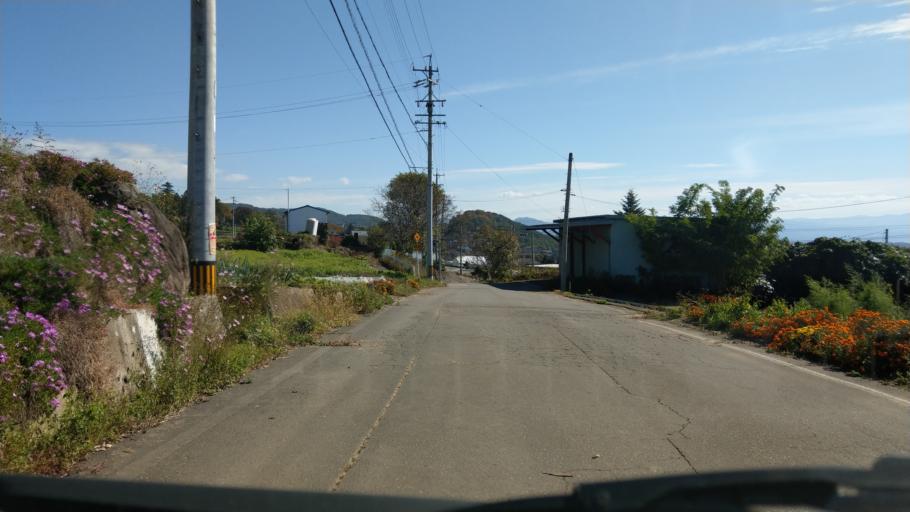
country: JP
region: Nagano
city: Komoro
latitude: 36.3520
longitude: 138.4048
